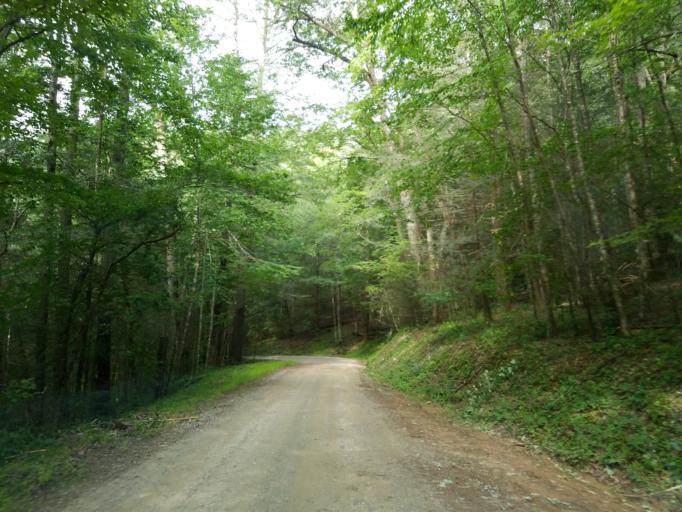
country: US
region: Georgia
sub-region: Union County
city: Blairsville
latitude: 34.7536
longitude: -84.0681
